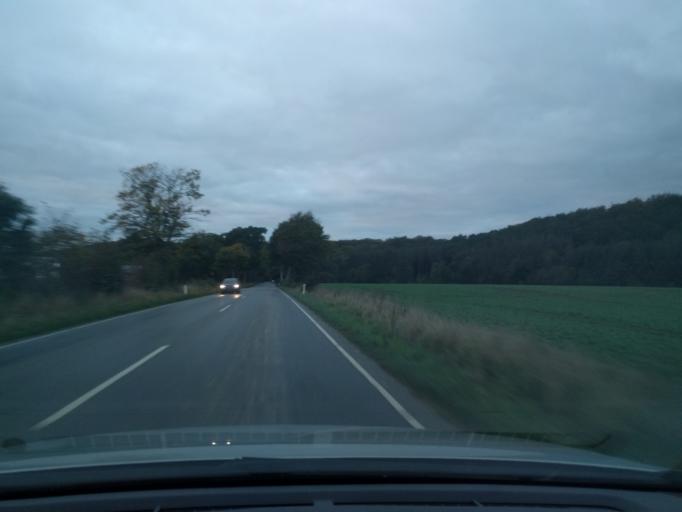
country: DK
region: South Denmark
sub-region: Odense Kommune
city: Bellinge
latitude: 55.2210
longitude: 10.2965
